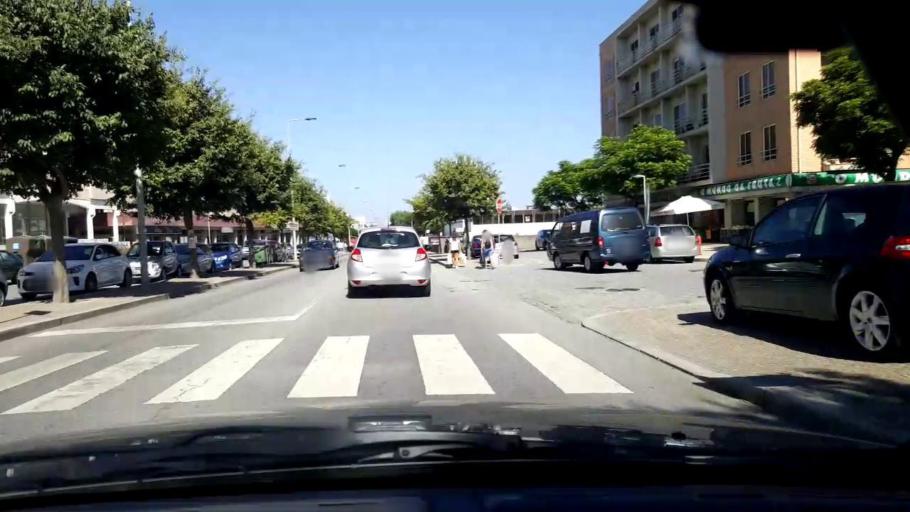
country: PT
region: Porto
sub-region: Vila do Conde
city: Vila do Conde
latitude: 41.3693
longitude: -8.7518
